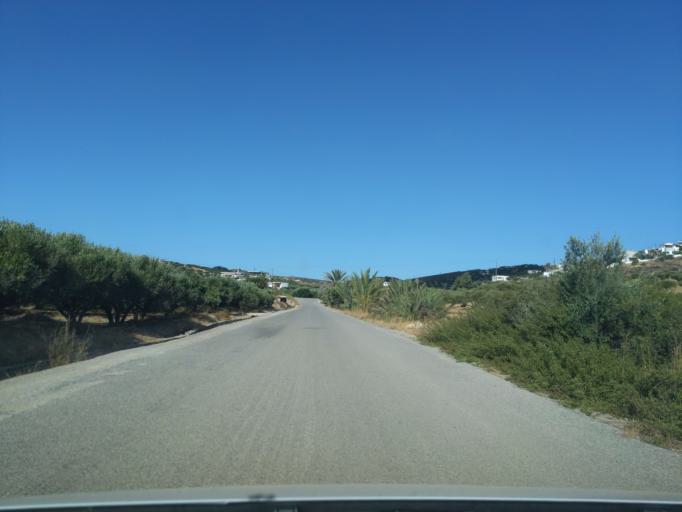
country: GR
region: Crete
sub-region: Nomos Lasithiou
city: Palekastro
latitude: 35.2157
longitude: 26.2664
